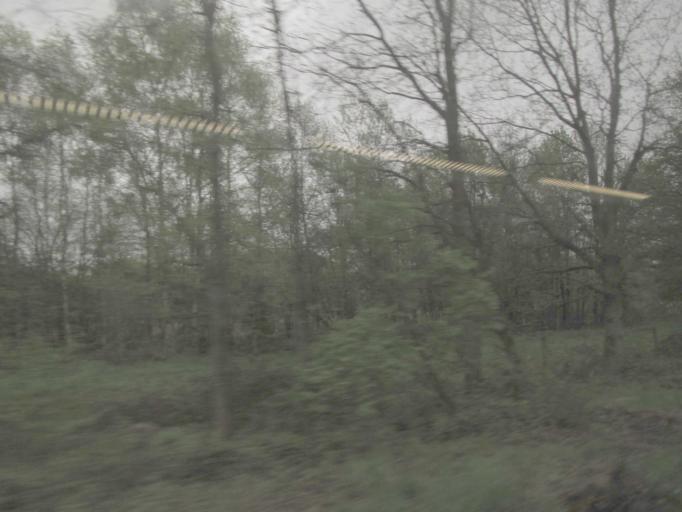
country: GB
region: England
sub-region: Surrey
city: Frimley
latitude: 51.3216
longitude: -0.7670
